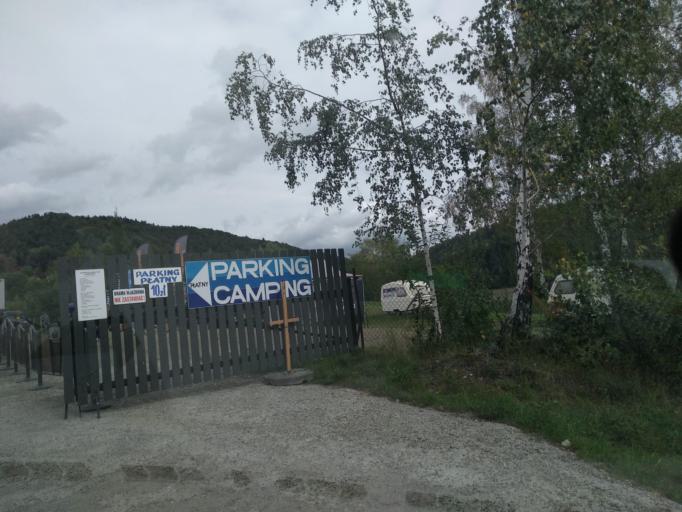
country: PL
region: Lesser Poland Voivodeship
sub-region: Powiat gorlicki
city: Ropa
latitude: 49.5526
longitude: 21.0809
